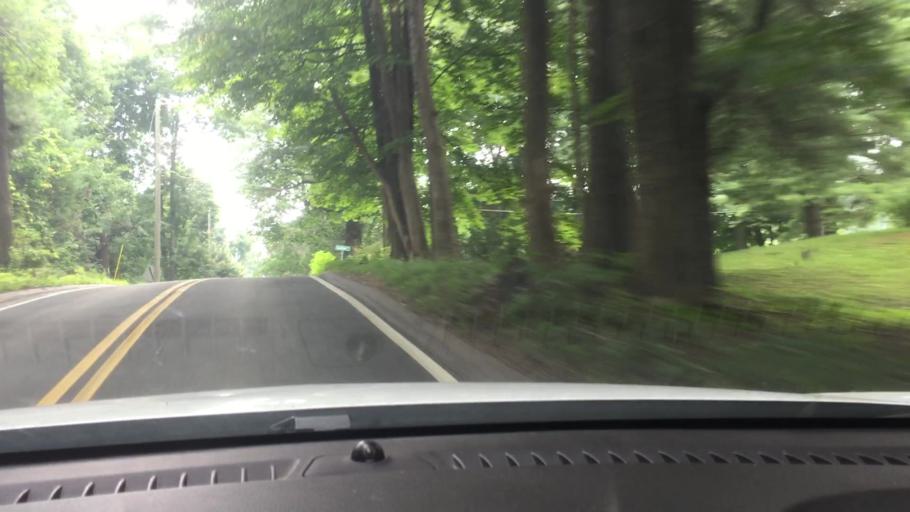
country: US
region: Massachusetts
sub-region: Berkshire County
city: Pittsfield
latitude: 42.4881
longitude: -73.2631
